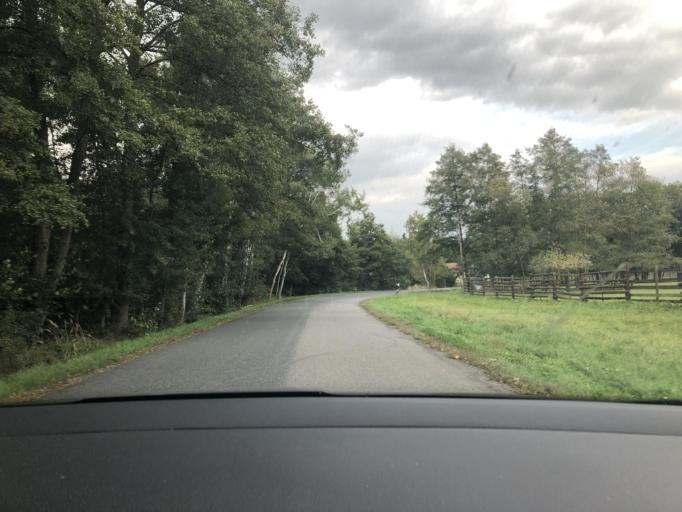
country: CZ
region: Pardubicky
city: Recany nad Labem
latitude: 50.0852
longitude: 15.4623
